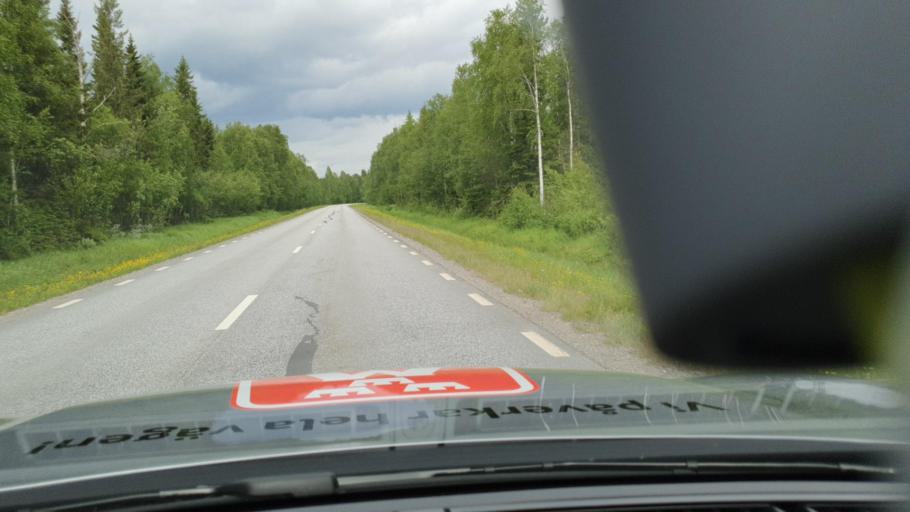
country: SE
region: Norrbotten
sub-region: Lulea Kommun
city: Lulea
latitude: 65.6893
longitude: 22.2093
